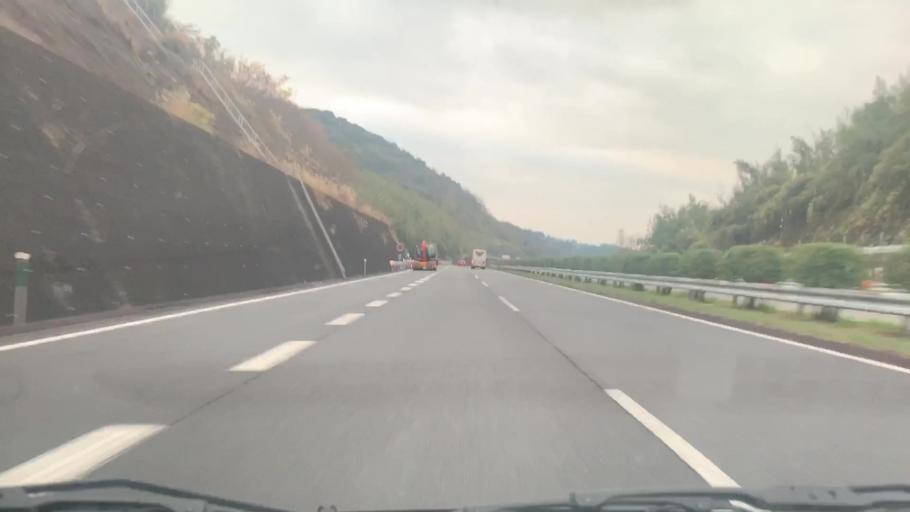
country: JP
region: Nagasaki
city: Omura
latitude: 32.9893
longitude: 129.9572
